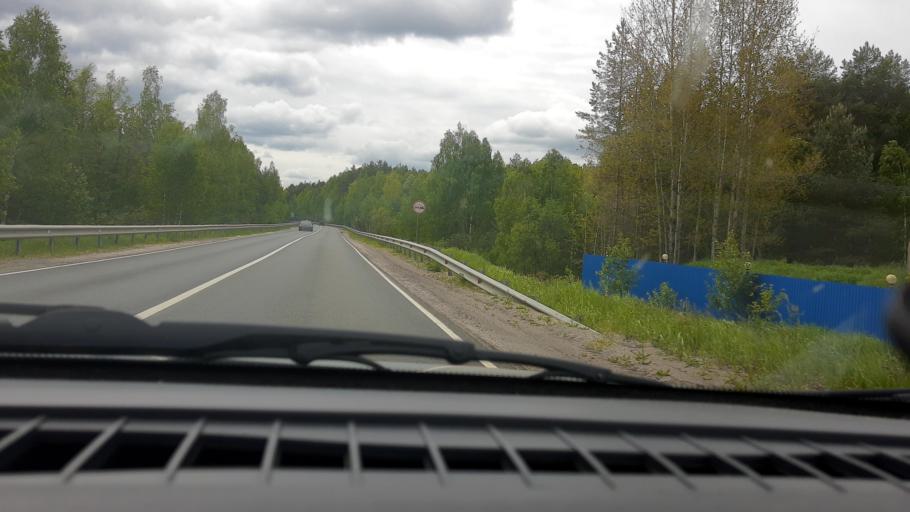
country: RU
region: Nizjnij Novgorod
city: Krasnyye Baki
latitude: 57.1385
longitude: 45.2212
